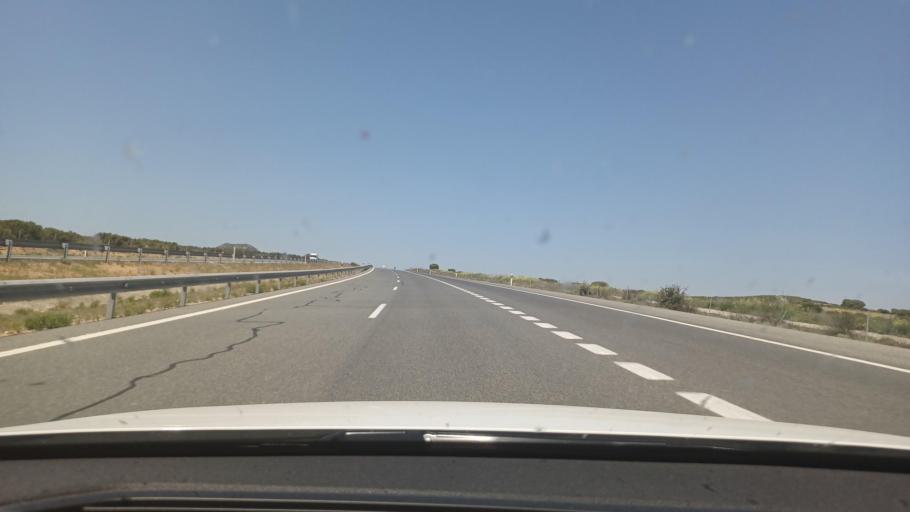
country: ES
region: Castille-La Mancha
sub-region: Provincia de Albacete
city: Higueruela
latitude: 38.8966
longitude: -1.4305
